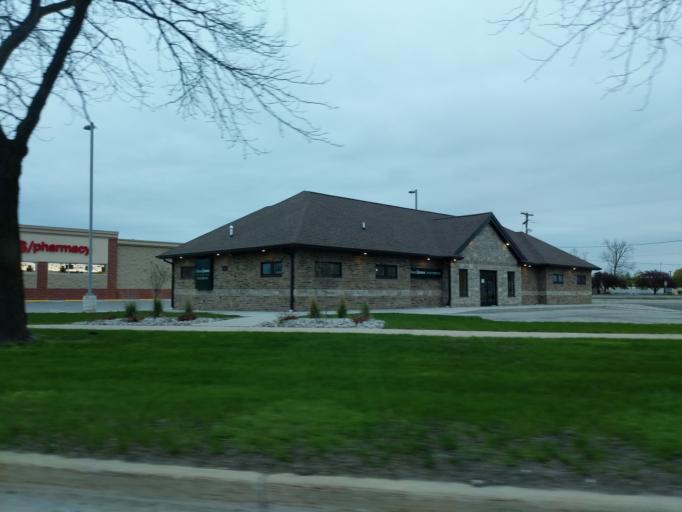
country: US
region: Michigan
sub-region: Midland County
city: Midland
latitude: 43.6185
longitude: -84.2183
